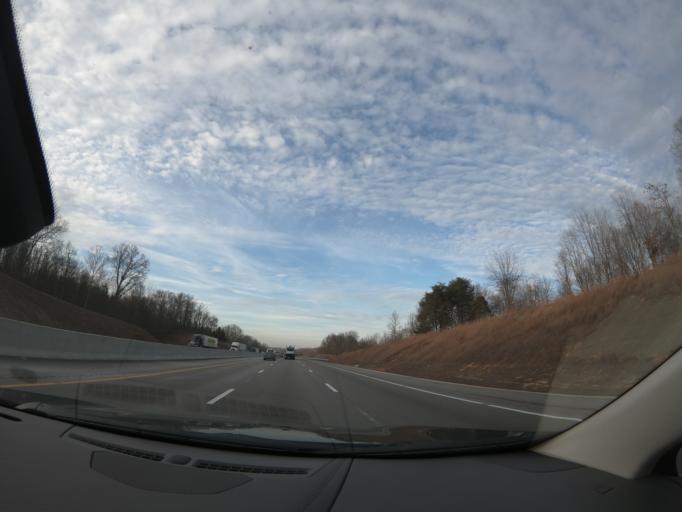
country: US
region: Kentucky
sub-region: Hart County
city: Munfordville
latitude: 37.3250
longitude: -85.9062
